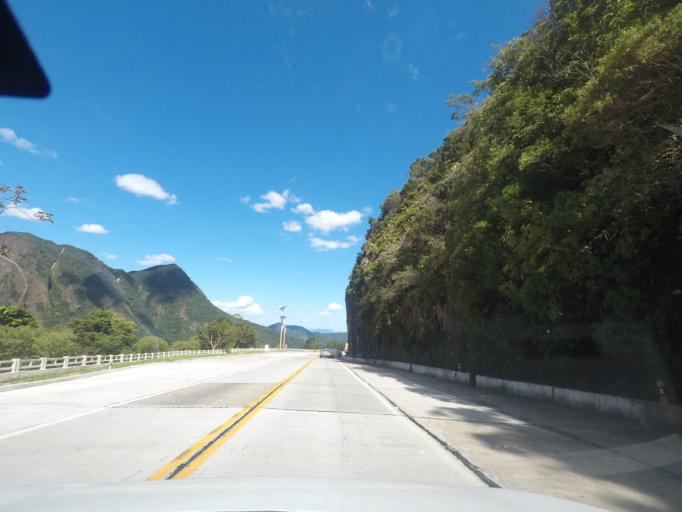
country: BR
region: Rio de Janeiro
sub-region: Teresopolis
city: Teresopolis
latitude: -22.4747
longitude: -42.9992
